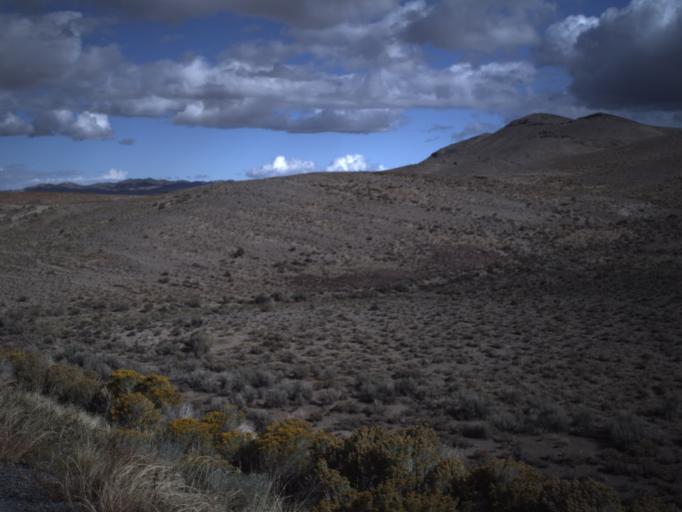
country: US
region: Utah
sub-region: Beaver County
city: Milford
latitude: 38.6182
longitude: -113.8454
